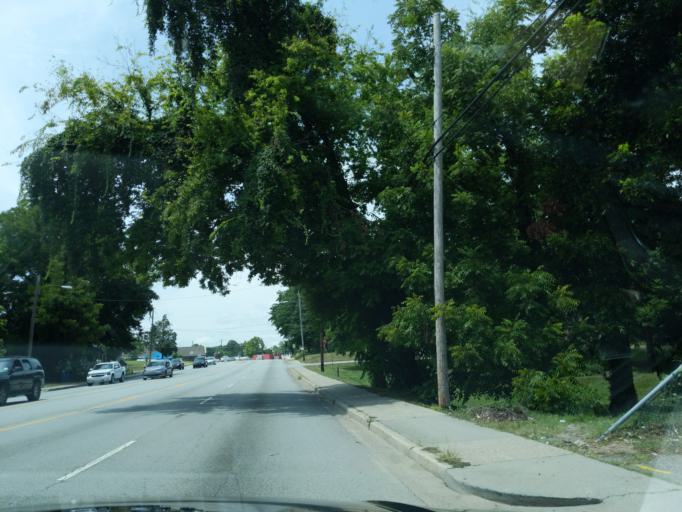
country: US
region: South Carolina
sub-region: Richland County
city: Forest Acres
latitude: 34.0331
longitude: -81.0210
